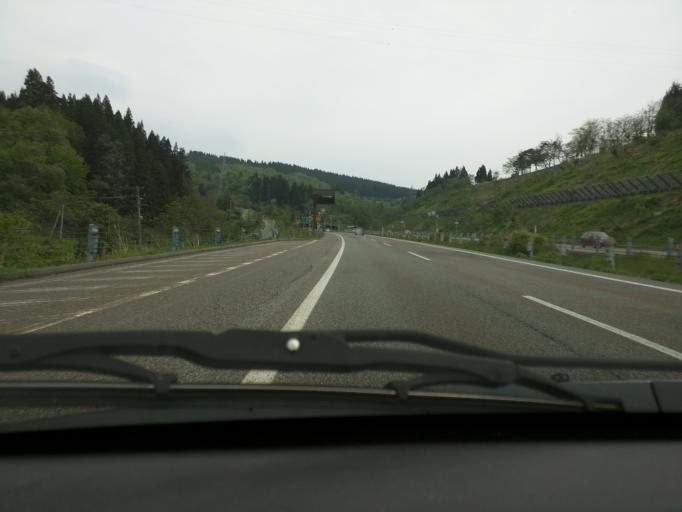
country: JP
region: Niigata
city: Ojiya
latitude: 37.2798
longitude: 138.7889
